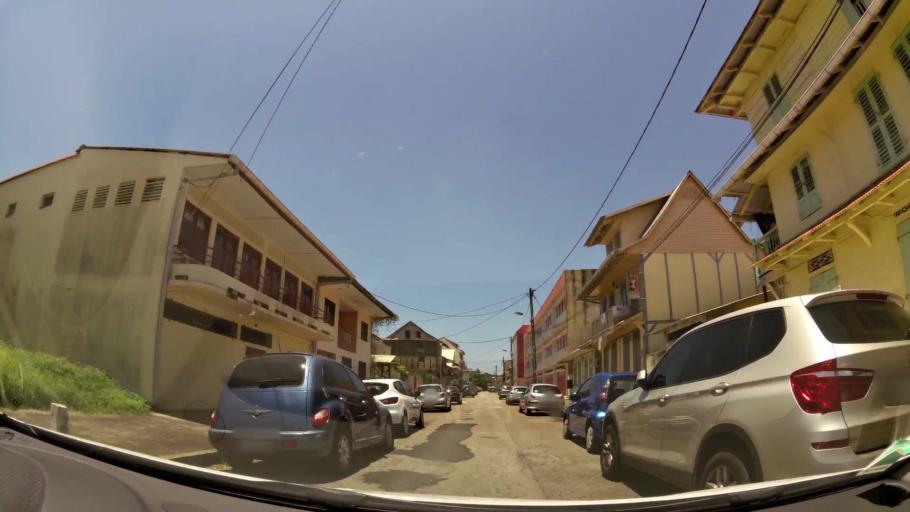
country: GF
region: Guyane
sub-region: Guyane
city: Cayenne
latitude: 4.9423
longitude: -52.3312
